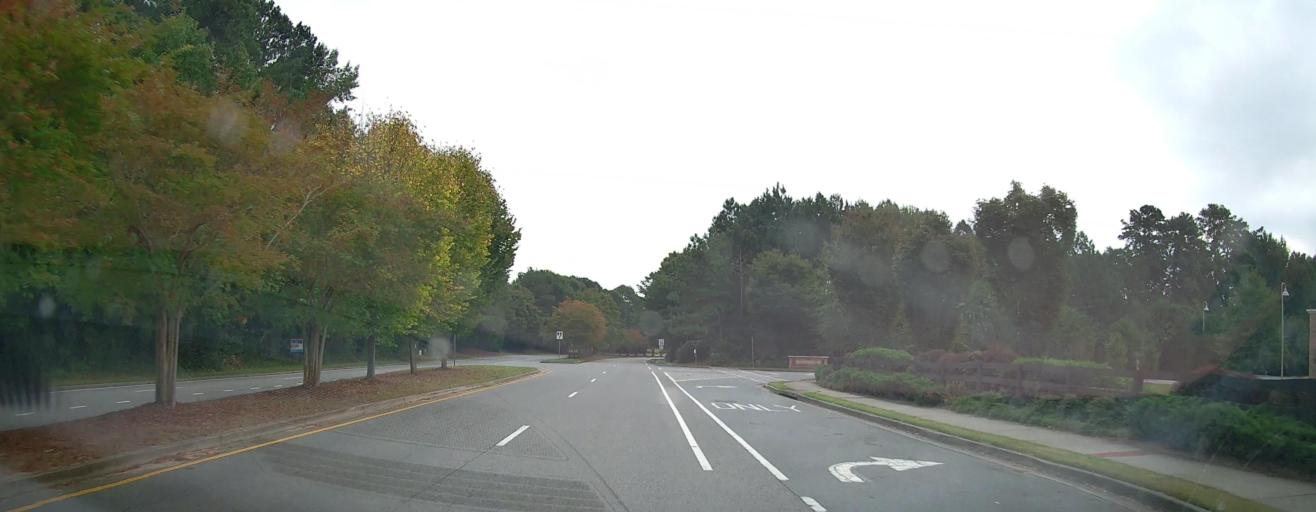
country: US
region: Georgia
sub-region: Fulton County
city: Alpharetta
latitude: 34.1064
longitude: -84.2687
